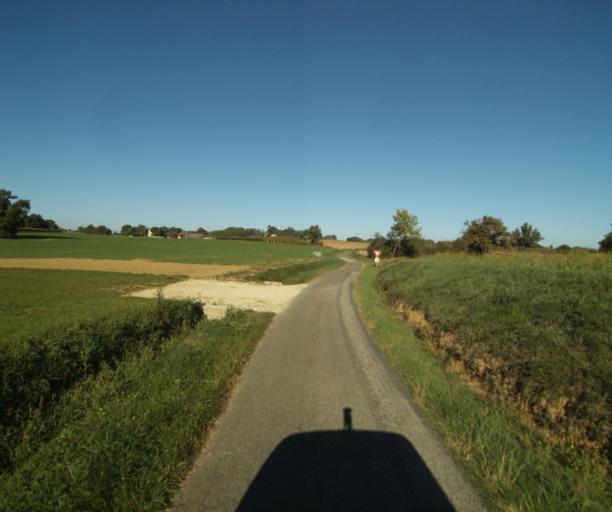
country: FR
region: Midi-Pyrenees
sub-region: Departement du Gers
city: Gondrin
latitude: 43.8414
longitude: 0.2653
